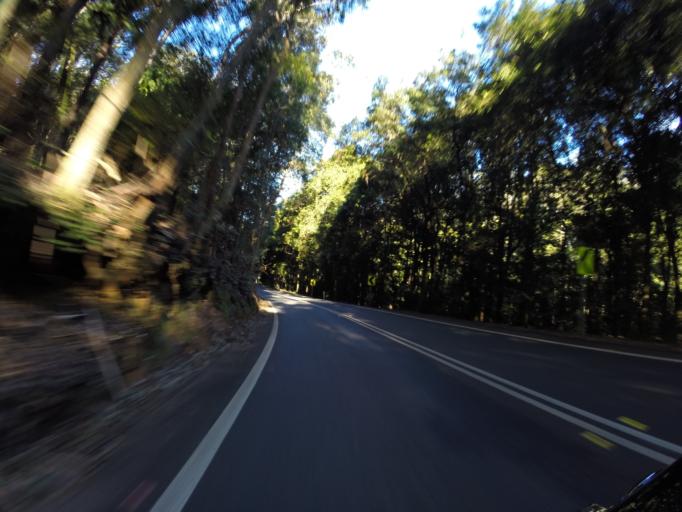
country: AU
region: New South Wales
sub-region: Wollongong
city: Helensburgh
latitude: -34.1693
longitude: 151.0170
